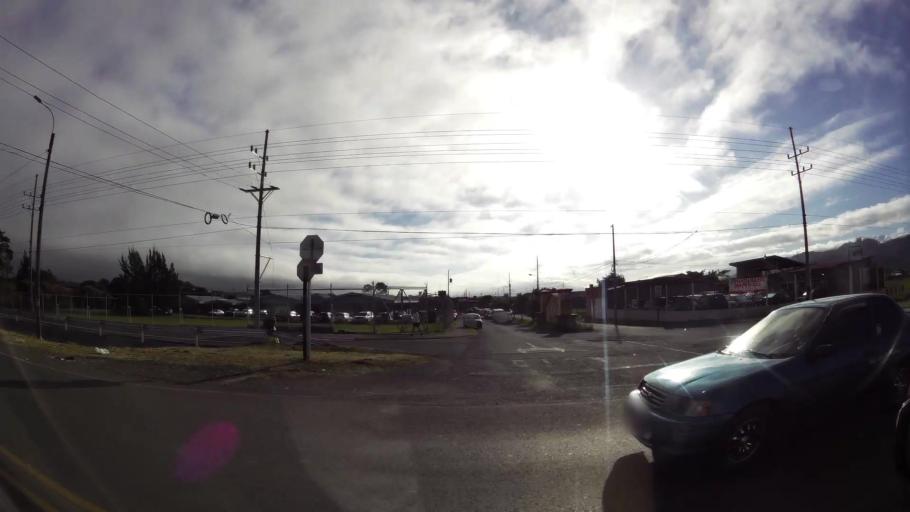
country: CR
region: Cartago
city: Cartago
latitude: 9.8523
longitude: -83.9485
